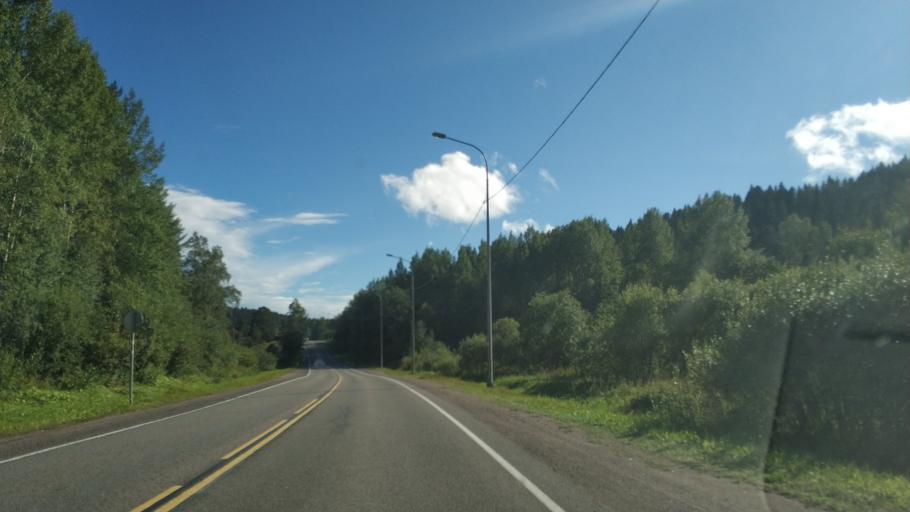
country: RU
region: Republic of Karelia
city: Sortavala
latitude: 61.6667
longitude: 30.6539
